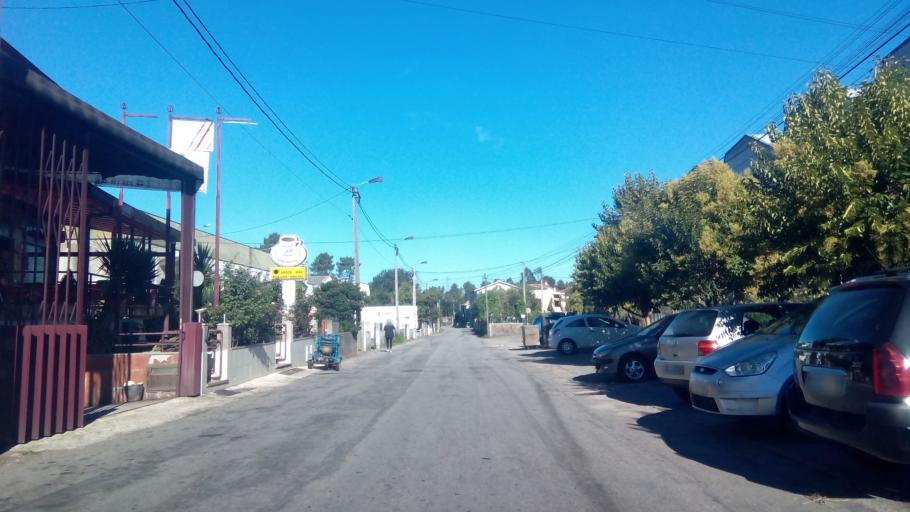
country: PT
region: Porto
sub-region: Paredes
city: Gandra
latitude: 41.1885
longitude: -8.4425
